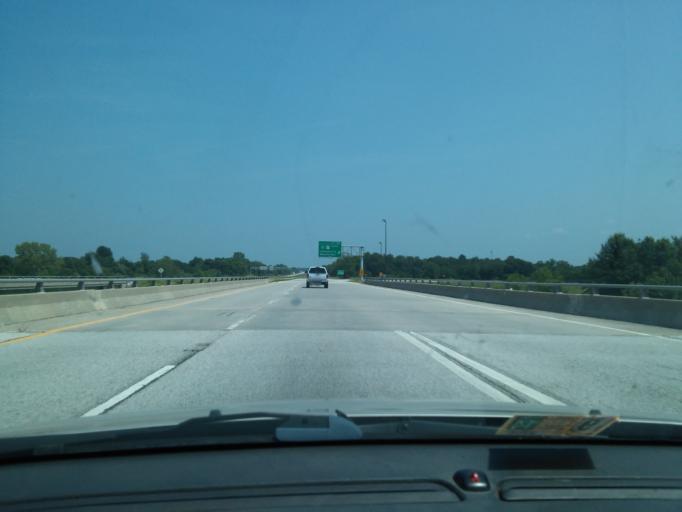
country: US
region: Illinois
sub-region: Morgan County
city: South Jacksonville
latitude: 39.6802
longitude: -90.2952
